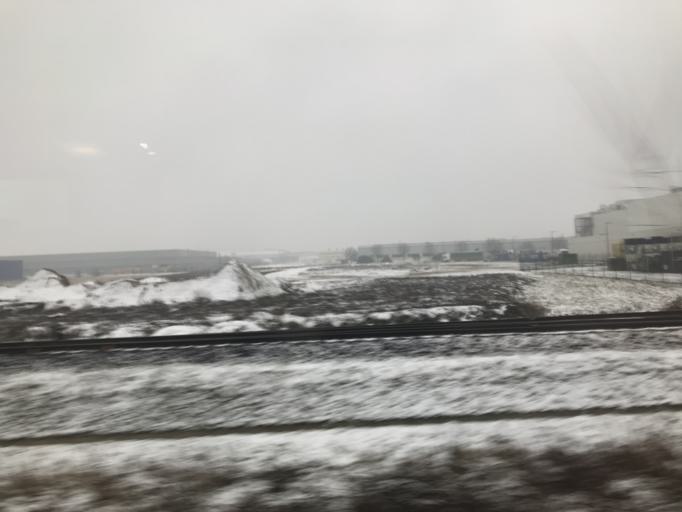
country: HU
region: Gyor-Moson-Sopron
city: Toltestava
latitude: 47.6836
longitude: 17.7048
